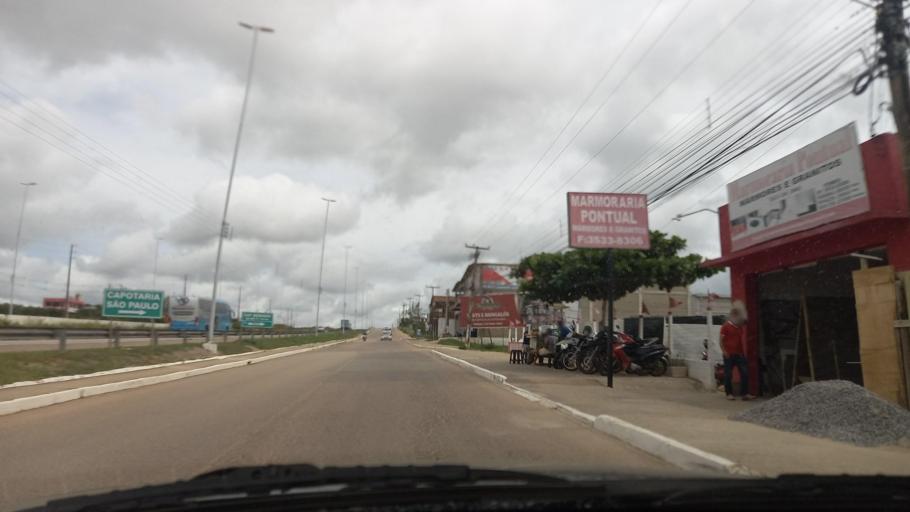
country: ET
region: Oromiya
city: Gore
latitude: 8.1970
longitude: 35.5793
